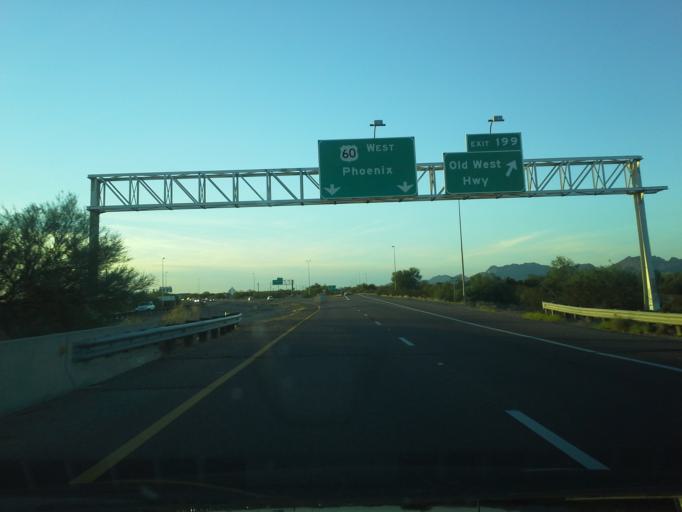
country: US
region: Arizona
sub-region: Pinal County
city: Apache Junction
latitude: 33.3856
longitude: -111.4993
